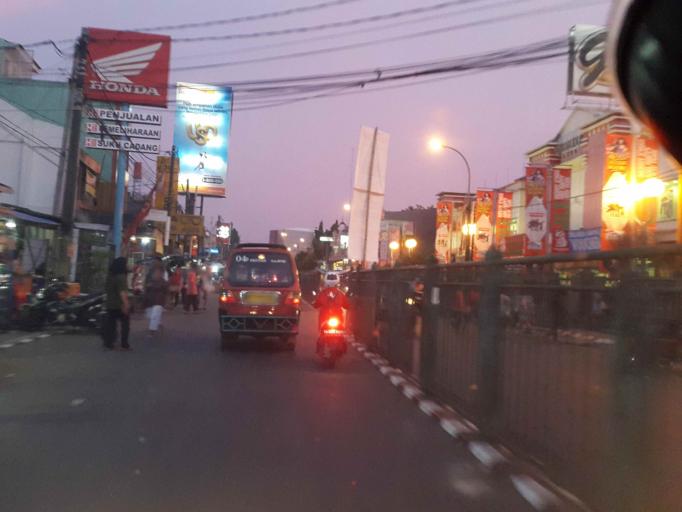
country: ID
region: West Java
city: Bekasi
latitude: -6.2478
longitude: 107.0115
